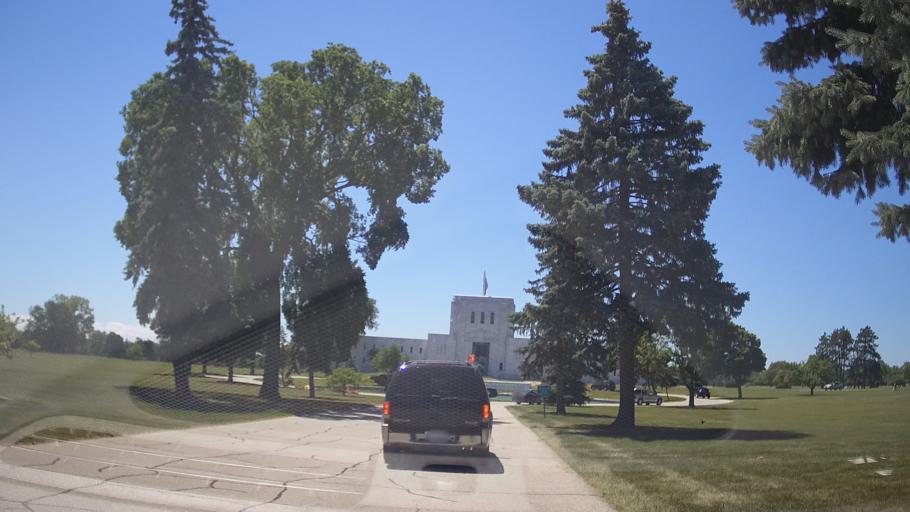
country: US
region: Michigan
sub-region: Oakland County
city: Troy
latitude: 42.5861
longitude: -83.1636
